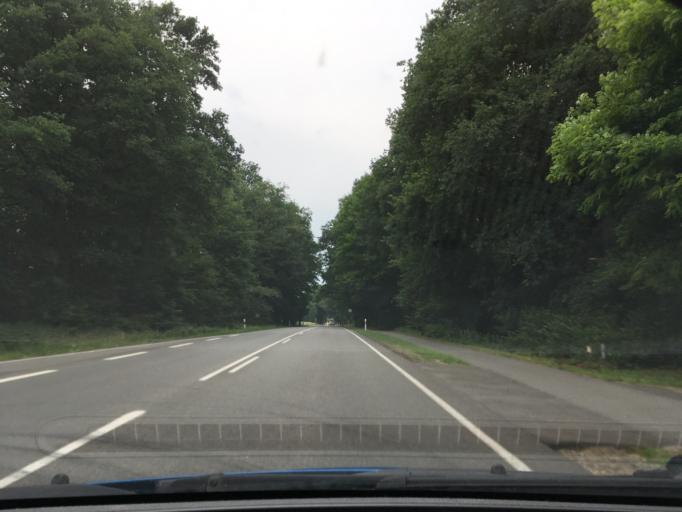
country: DE
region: Lower Saxony
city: Appel
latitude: 53.3916
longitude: 9.7941
